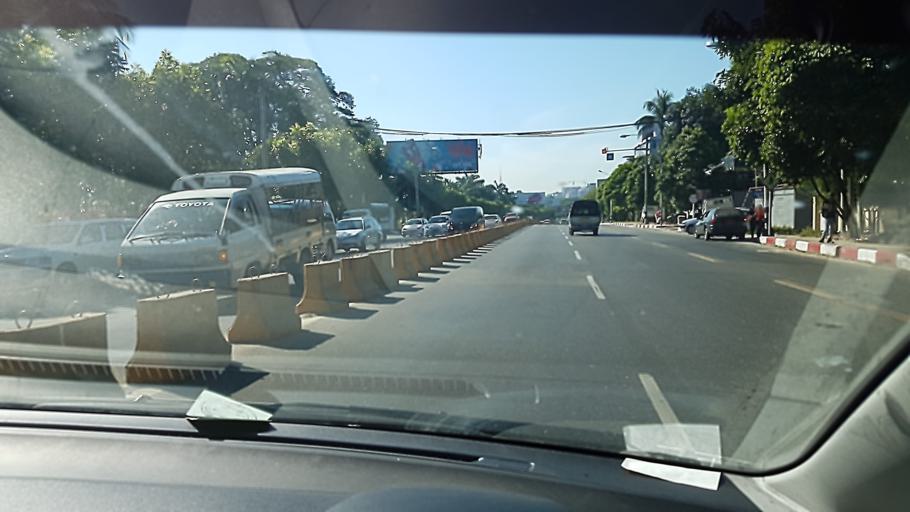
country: MM
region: Yangon
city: Yangon
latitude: 16.8427
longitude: 96.1355
